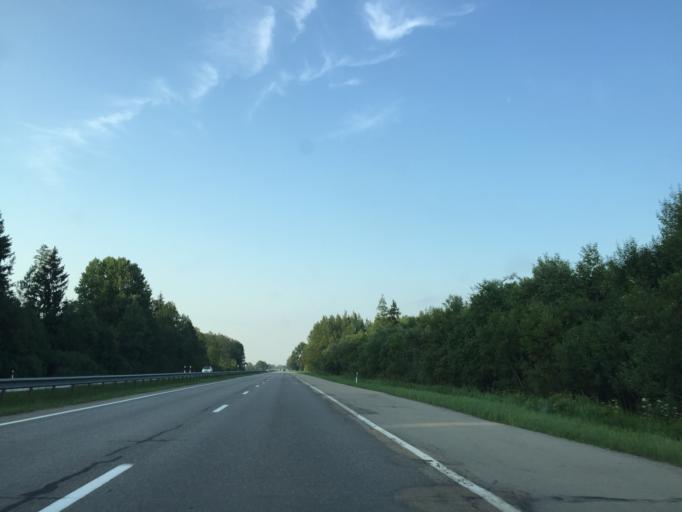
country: LV
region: Olaine
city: Olaine
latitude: 56.7577
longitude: 23.9043
